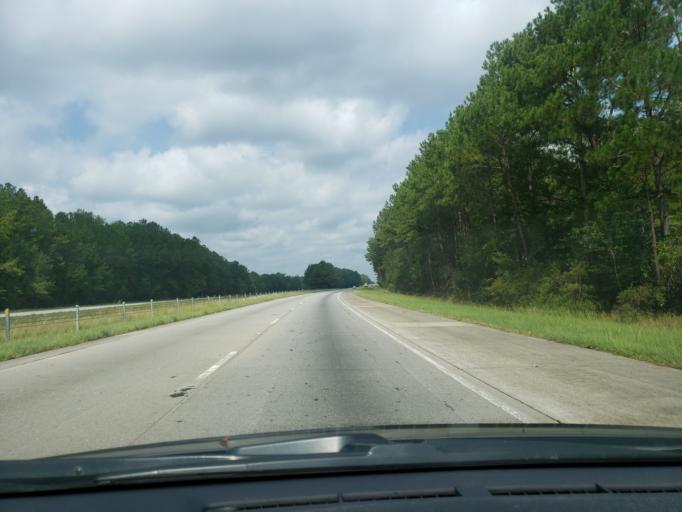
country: US
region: Georgia
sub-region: Emanuel County
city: Swainsboro
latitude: 32.4082
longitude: -82.3477
